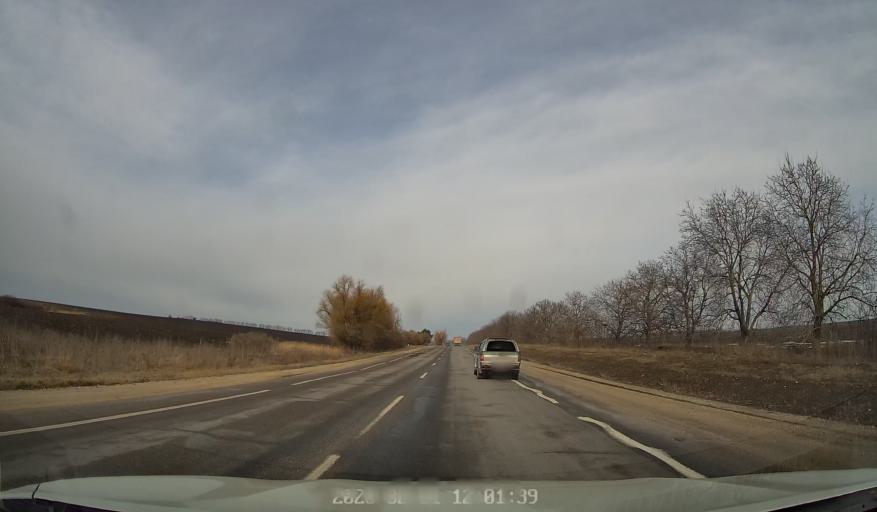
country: MD
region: Riscani
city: Riscani
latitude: 47.9412
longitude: 27.6271
